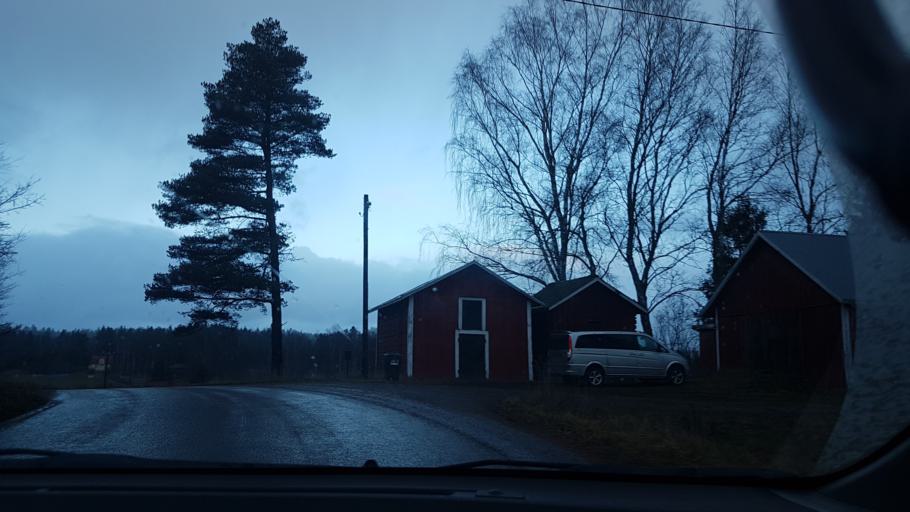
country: FI
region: Uusimaa
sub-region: Helsinki
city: Lohja
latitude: 60.2124
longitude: 24.1009
